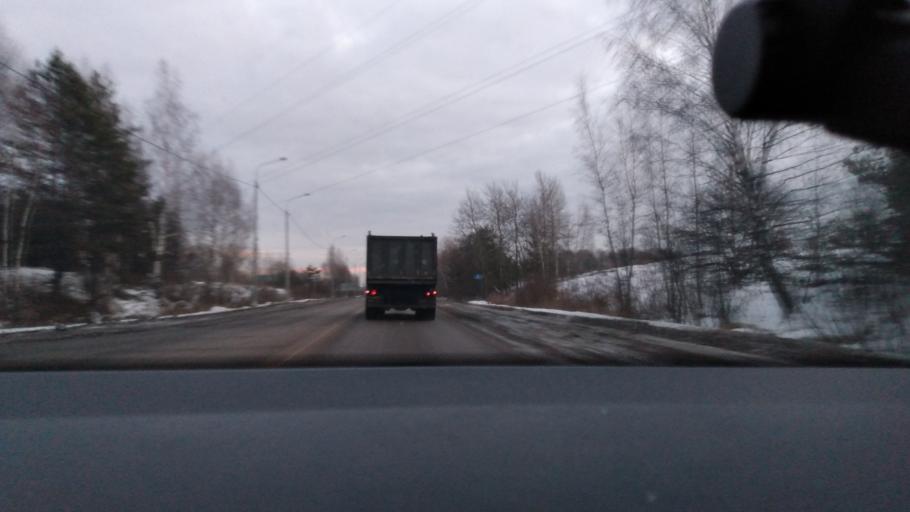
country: RU
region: Moskovskaya
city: Yegor'yevsk
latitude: 55.4142
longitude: 39.0468
